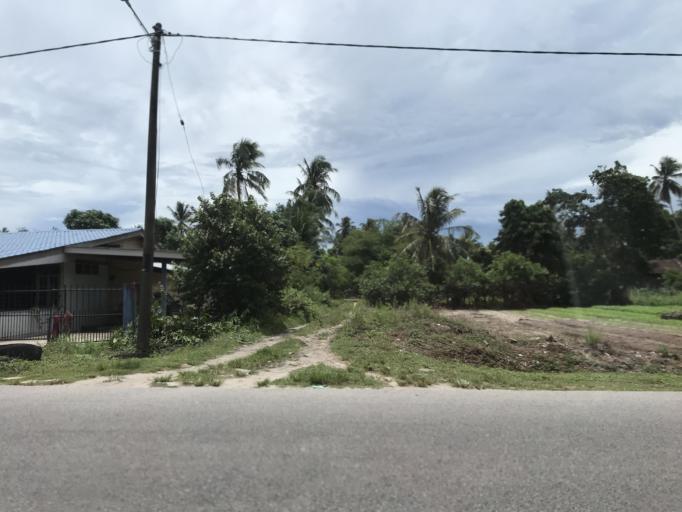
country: MY
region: Kelantan
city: Tumpat
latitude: 6.1787
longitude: 102.1822
